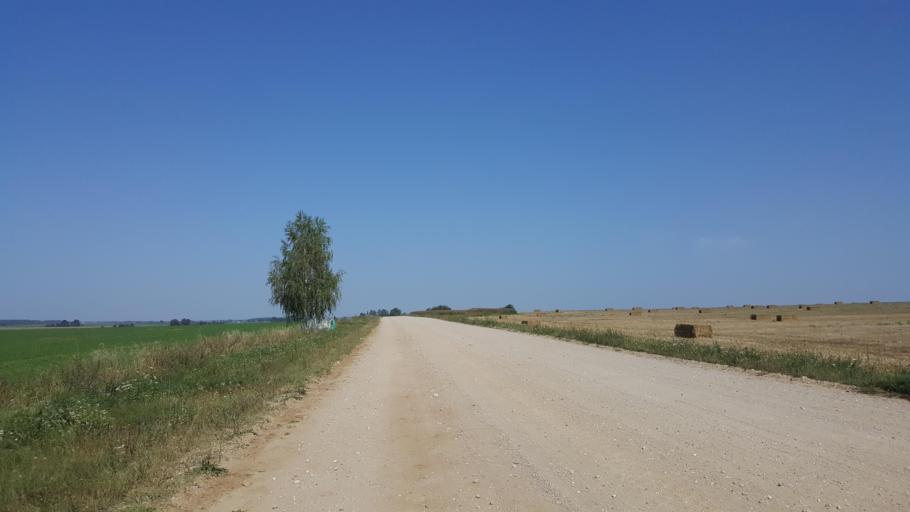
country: BY
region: Brest
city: Vysokaye
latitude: 52.4514
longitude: 23.4445
